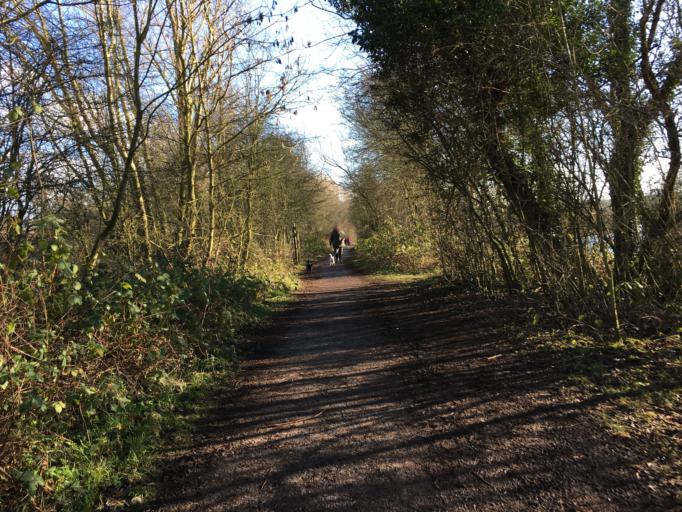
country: GB
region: England
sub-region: Nottinghamshire
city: Gotham
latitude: 52.9080
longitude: -1.2189
